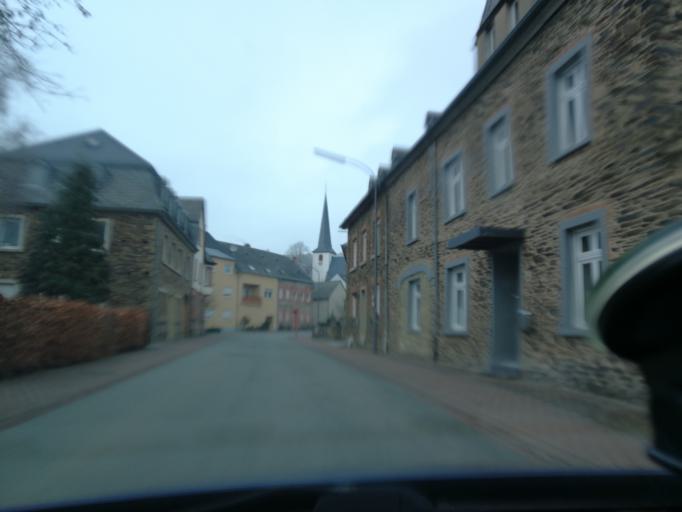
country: DE
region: Rheinland-Pfalz
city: Osann-Monzel
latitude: 49.9194
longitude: 6.9524
